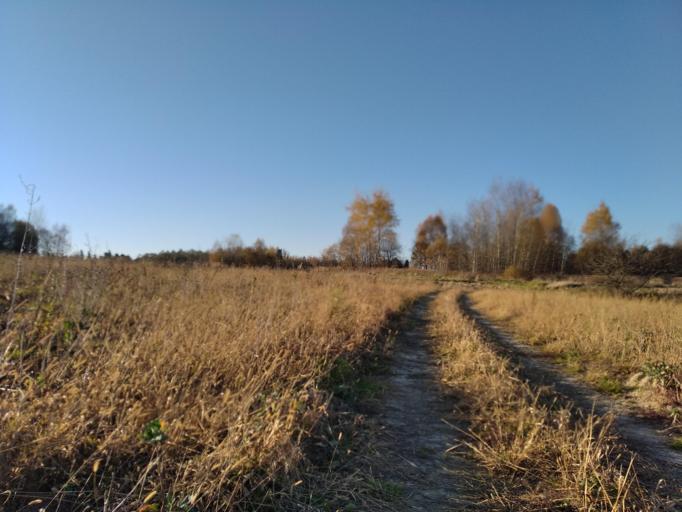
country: PL
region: Subcarpathian Voivodeship
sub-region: Powiat strzyzowski
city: Strzyzow
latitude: 49.8390
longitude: 21.7983
